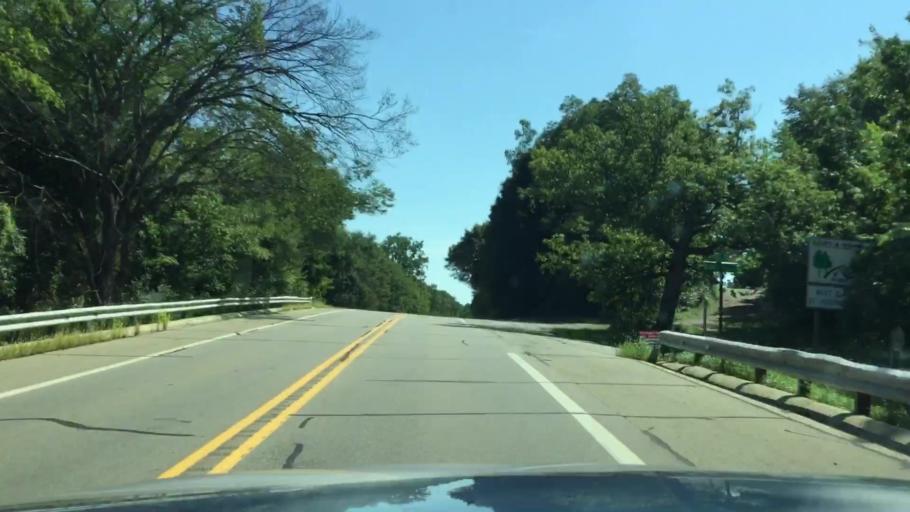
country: US
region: Michigan
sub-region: Jackson County
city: Brooklyn
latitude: 42.0596
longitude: -84.1801
